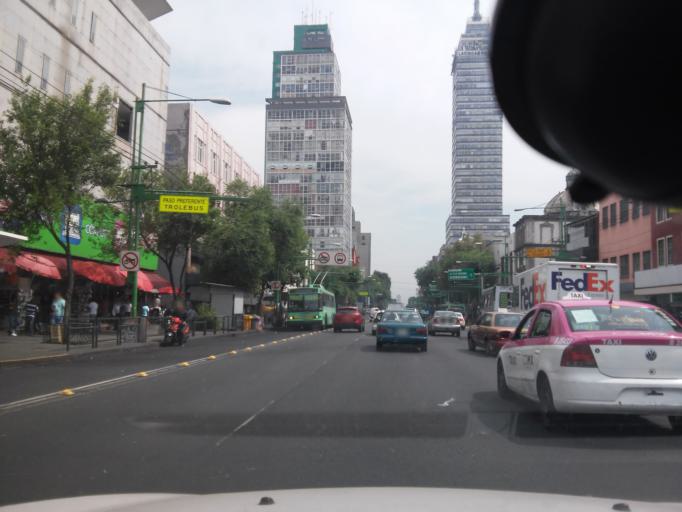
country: MX
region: Mexico City
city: Mexico City
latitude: 19.4313
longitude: -99.1414
